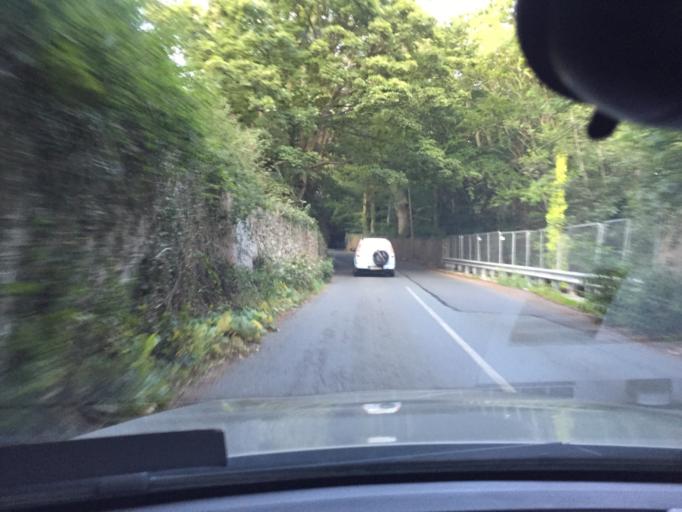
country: IE
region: Leinster
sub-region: Wicklow
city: Enniskerry
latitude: 53.1854
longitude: -6.1730
